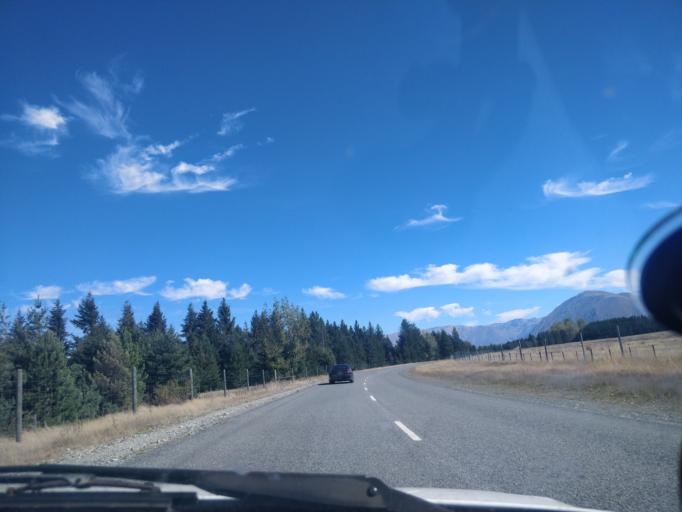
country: NZ
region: Otago
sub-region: Queenstown-Lakes District
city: Wanaka
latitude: -44.2720
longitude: 170.0596
